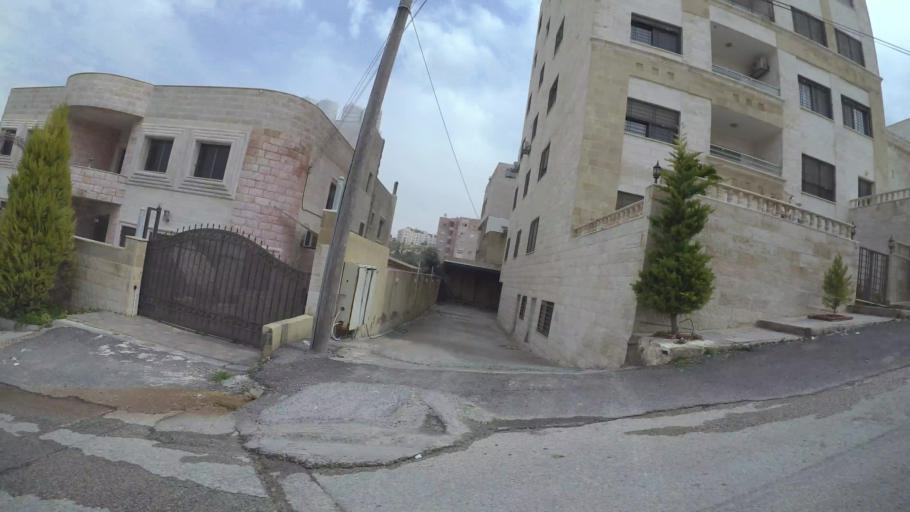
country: JO
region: Amman
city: Umm as Summaq
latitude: 31.8992
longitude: 35.8305
